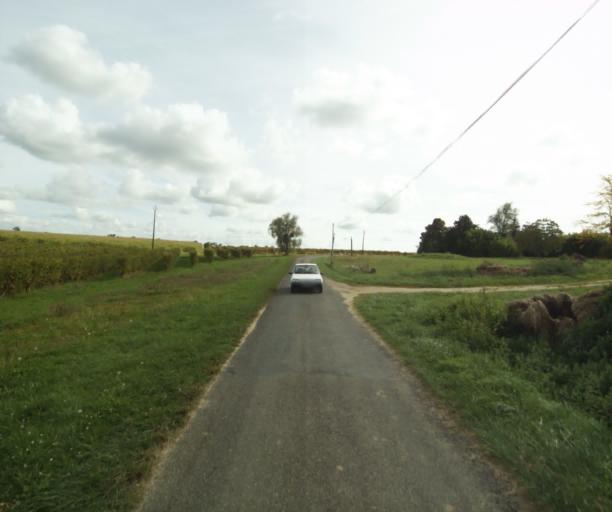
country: FR
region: Midi-Pyrenees
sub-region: Departement du Gers
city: Eauze
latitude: 43.8656
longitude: 0.0778
